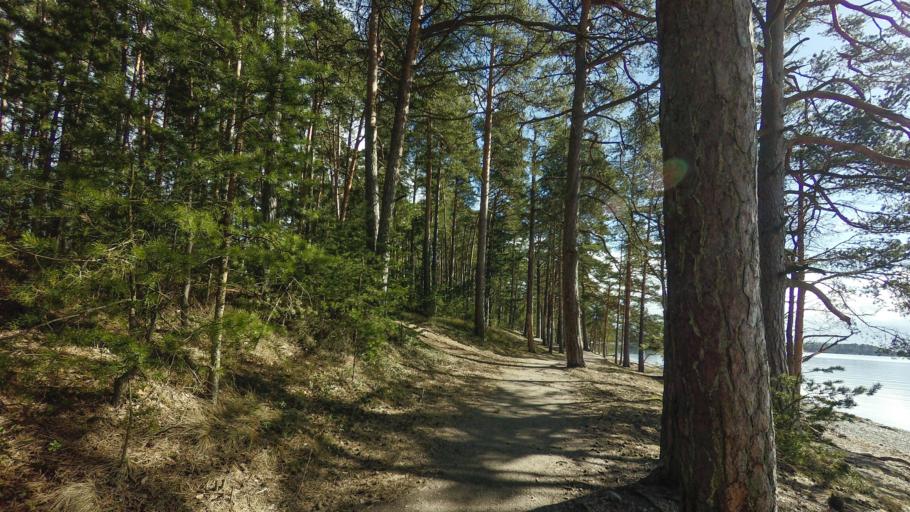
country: FI
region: Uusimaa
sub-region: Helsinki
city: Vantaa
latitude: 60.1975
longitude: 25.1325
